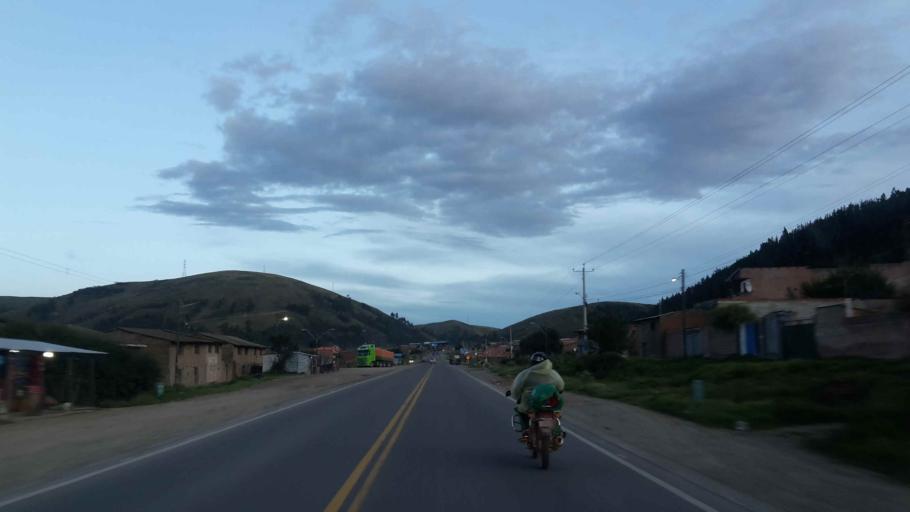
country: BO
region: Cochabamba
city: Colomi
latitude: -17.3644
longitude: -65.8408
